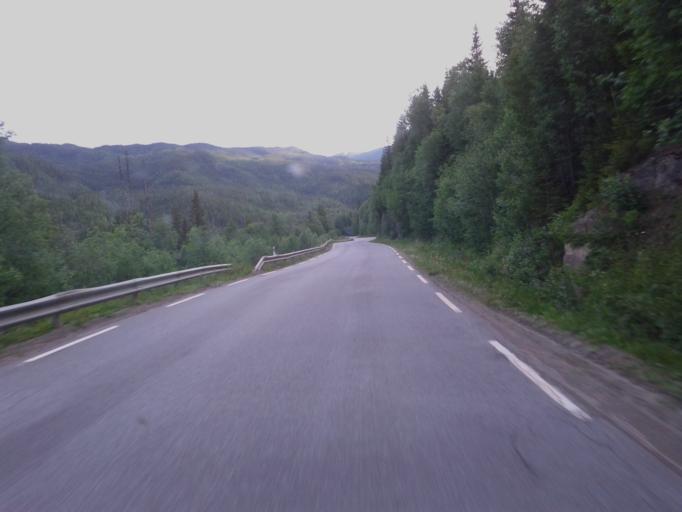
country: NO
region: Nordland
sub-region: Grane
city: Trofors
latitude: 65.5226
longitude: 13.6425
